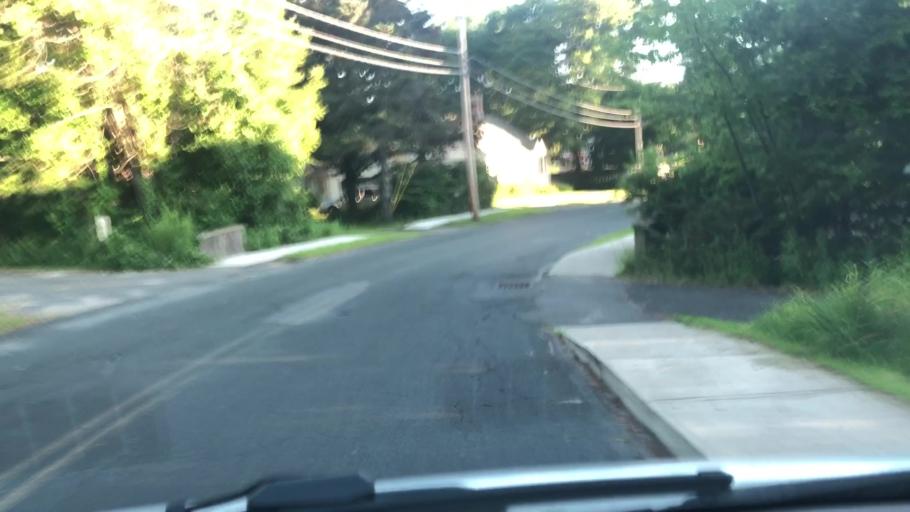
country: US
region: Massachusetts
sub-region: Hampshire County
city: Williamsburg
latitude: 42.3905
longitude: -72.7292
